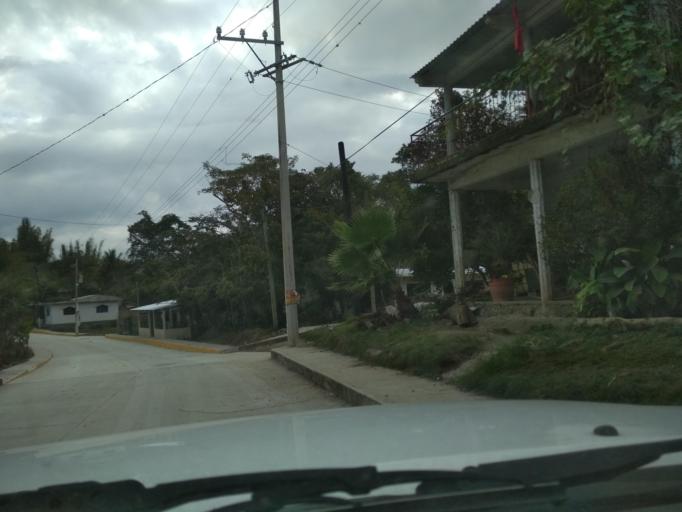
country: MX
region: Veracruz
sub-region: Coatepec
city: Tuzamapan
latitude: 19.3688
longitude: -96.8814
